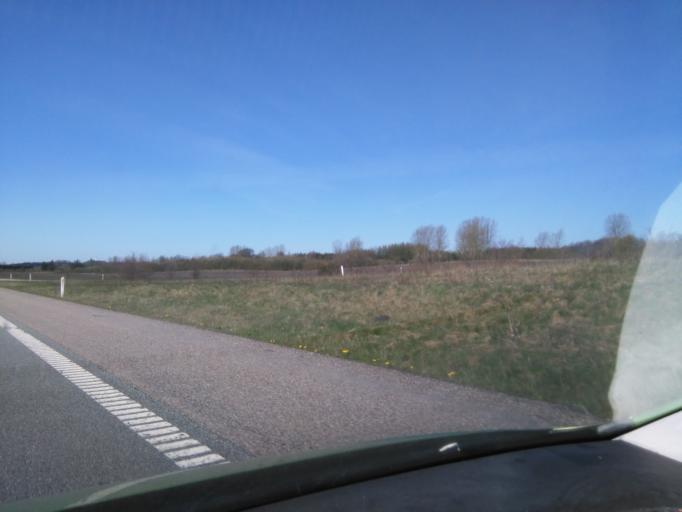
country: DK
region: South Denmark
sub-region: Vejle Kommune
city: Give
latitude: 55.8410
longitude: 9.2742
